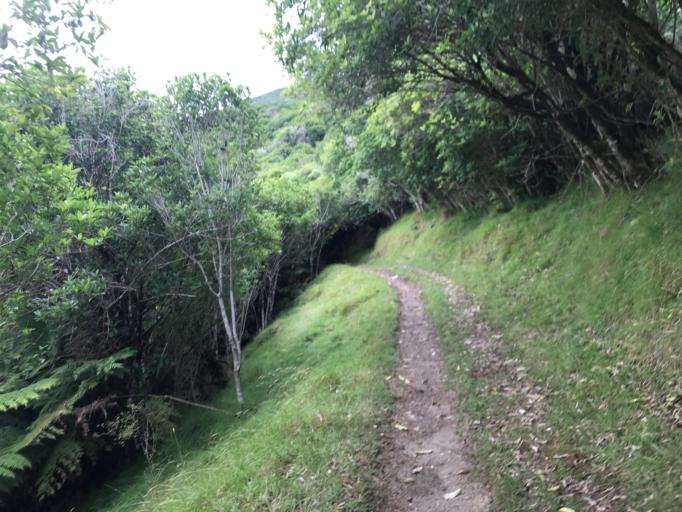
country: NZ
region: Marlborough
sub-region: Marlborough District
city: Picton
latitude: -41.2324
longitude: 173.9580
